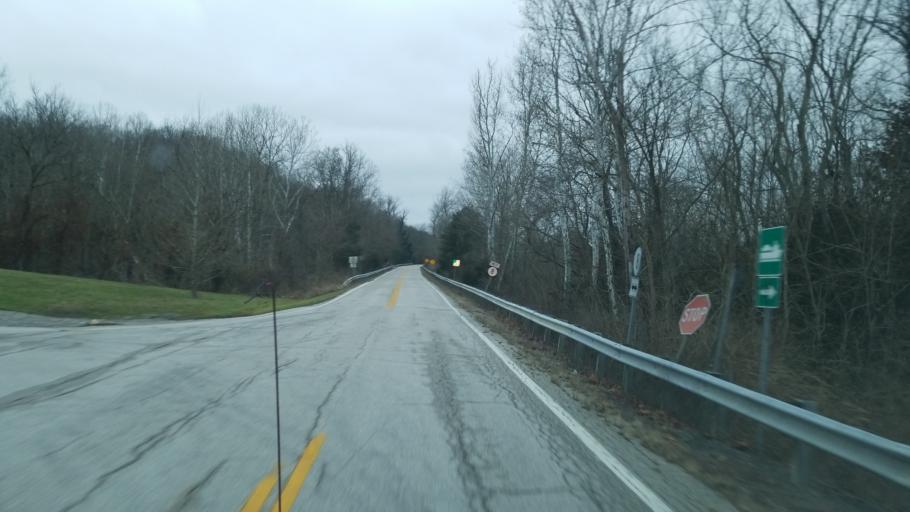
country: US
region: Kentucky
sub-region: Bracken County
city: Brooksville
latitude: 38.7696
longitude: -84.1038
